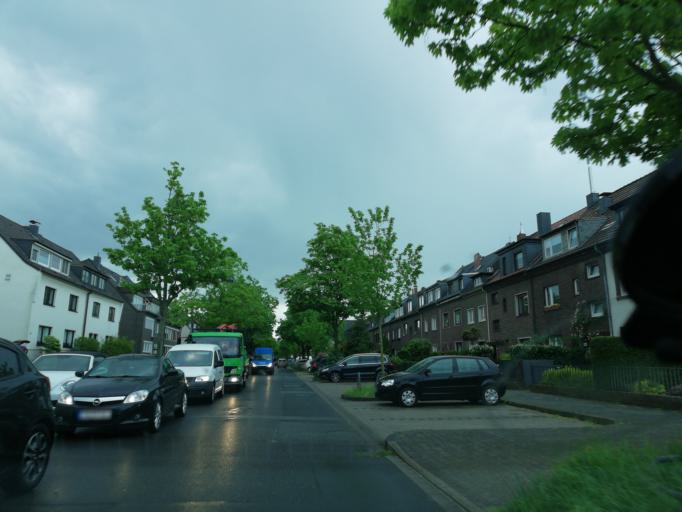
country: DE
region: North Rhine-Westphalia
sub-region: Regierungsbezirk Dusseldorf
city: Dusseldorf
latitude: 51.1995
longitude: 6.7627
